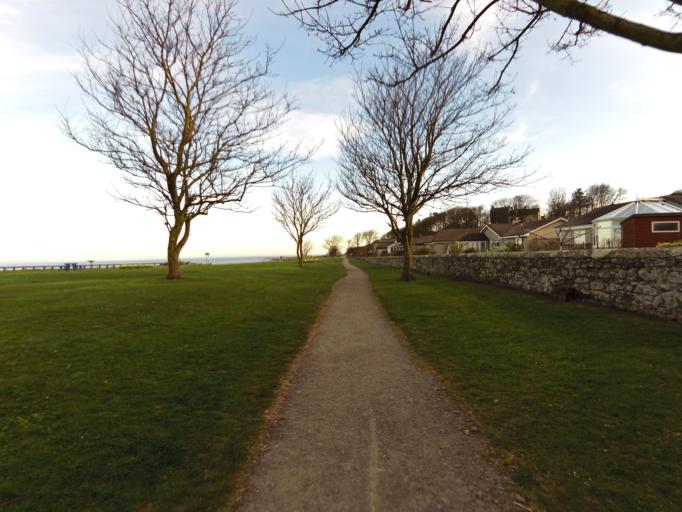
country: GB
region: Scotland
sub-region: Aberdeenshire
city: Inverbervie
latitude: 56.8419
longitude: -2.2764
